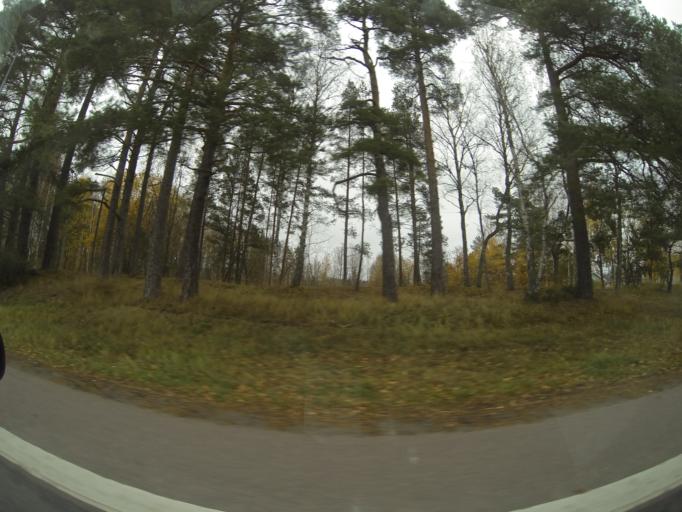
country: SE
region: Vaestmanland
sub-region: Surahammars Kommun
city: Ramnas
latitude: 59.7726
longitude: 16.1986
